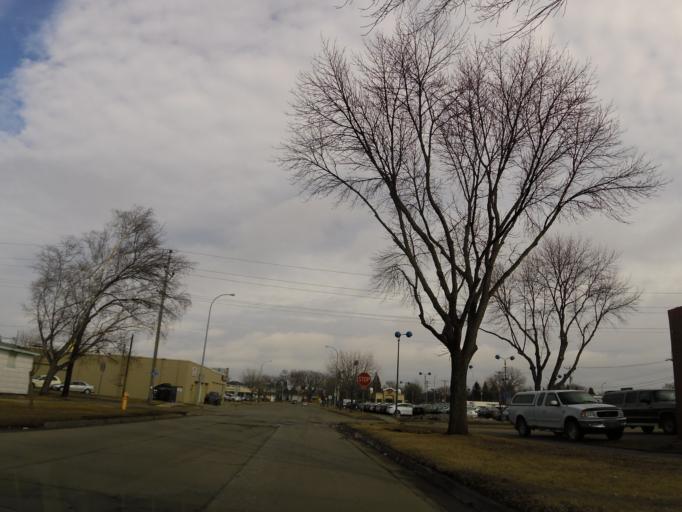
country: US
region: North Dakota
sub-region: Grand Forks County
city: Grand Forks
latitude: 47.9091
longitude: -97.0470
